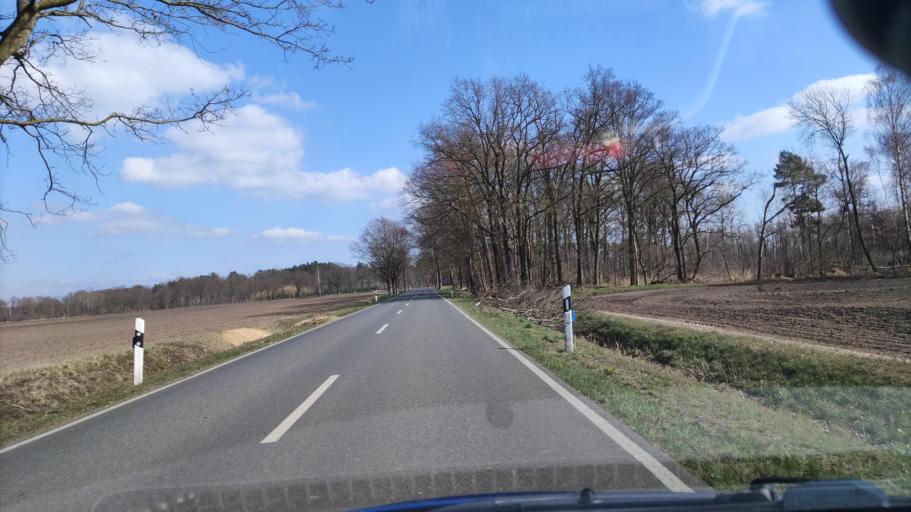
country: DE
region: Lower Saxony
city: Woltersdorf
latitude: 52.9972
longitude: 11.2197
